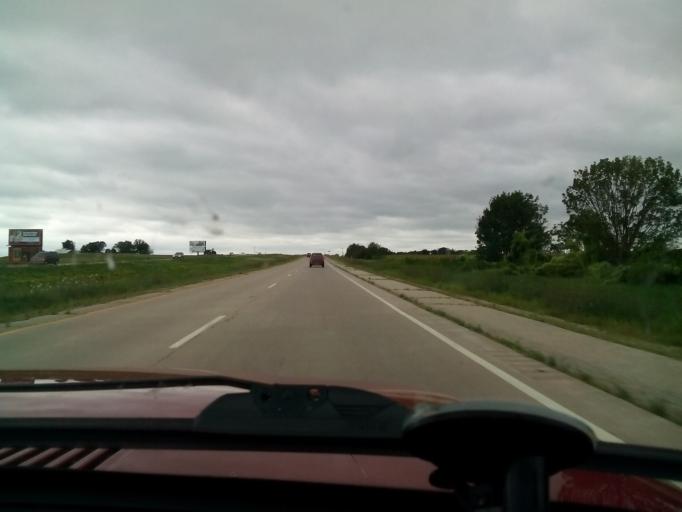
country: US
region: Wisconsin
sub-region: Columbia County
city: Columbus
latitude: 43.2952
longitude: -89.0648
